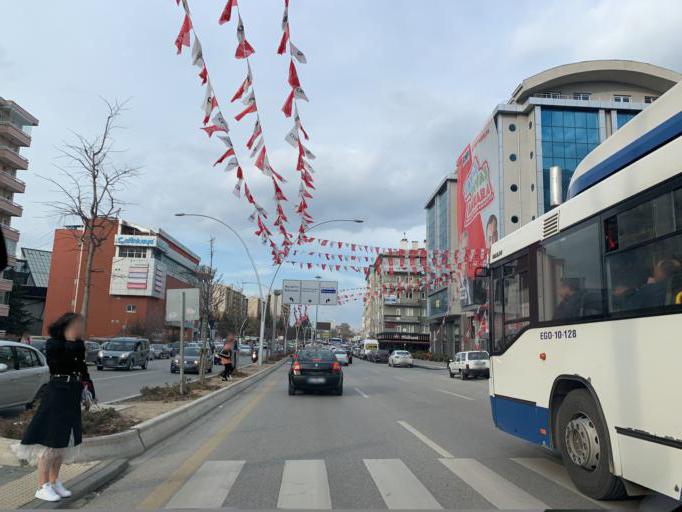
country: TR
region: Ankara
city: Cankaya
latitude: 39.8754
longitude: 32.8634
